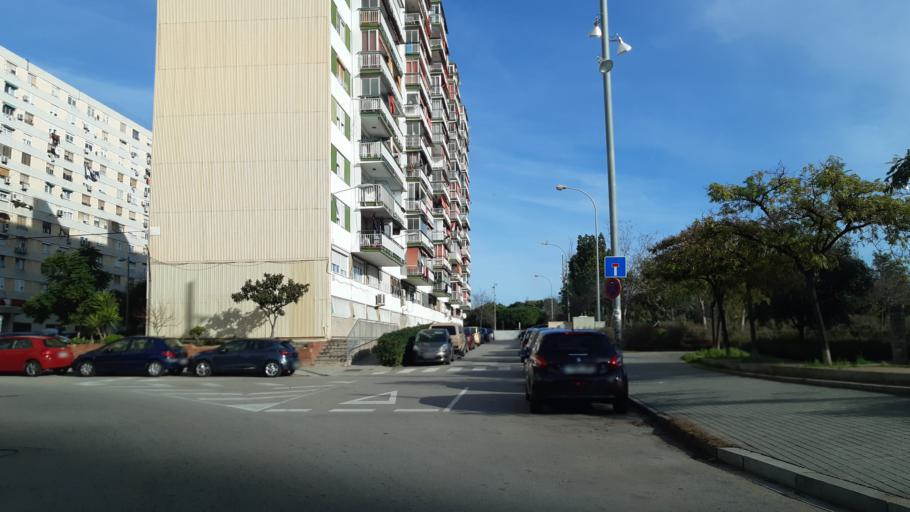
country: ES
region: Catalonia
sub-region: Provincia de Barcelona
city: L'Hospitalet de Llobregat
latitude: 41.3476
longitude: 2.1093
